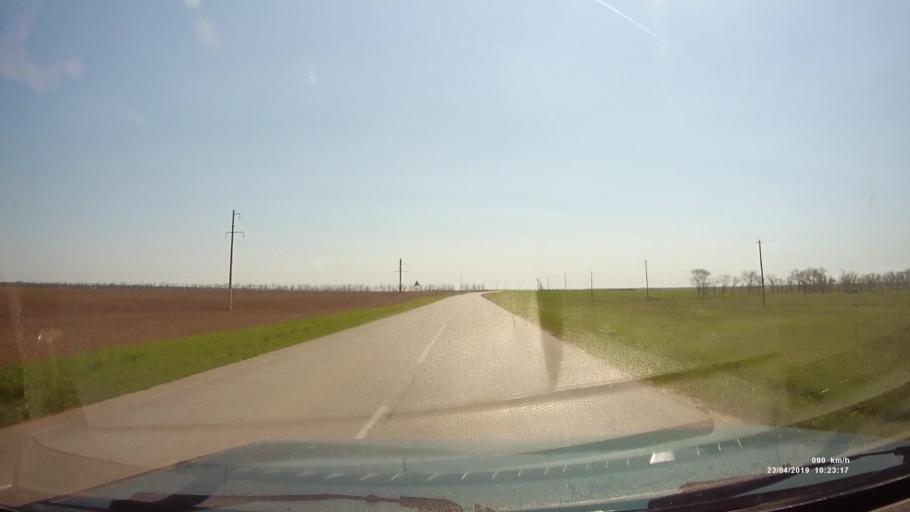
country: RU
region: Rostov
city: Sovetskoye
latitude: 46.6487
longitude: 42.4216
